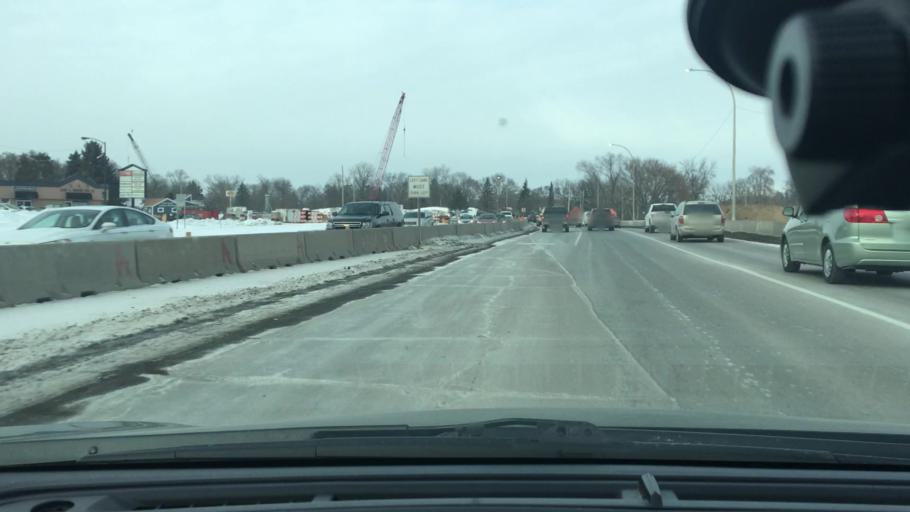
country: US
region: Minnesota
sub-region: Hennepin County
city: Champlin
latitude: 45.1837
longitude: -93.3922
